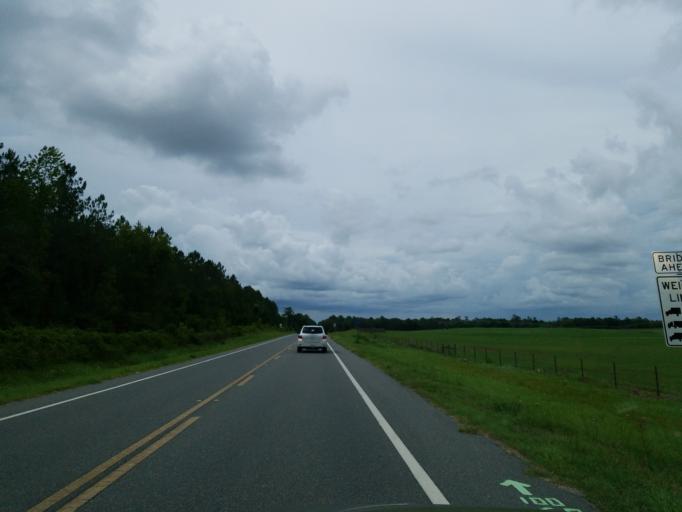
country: US
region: Florida
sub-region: Alachua County
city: High Springs
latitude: 29.9302
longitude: -82.5060
